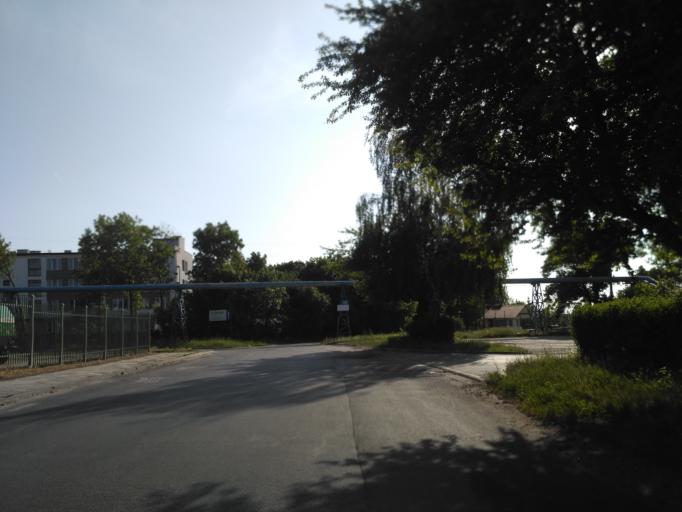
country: PL
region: Lublin Voivodeship
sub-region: Powiat lubelski
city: Lublin
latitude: 51.2131
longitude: 22.5582
